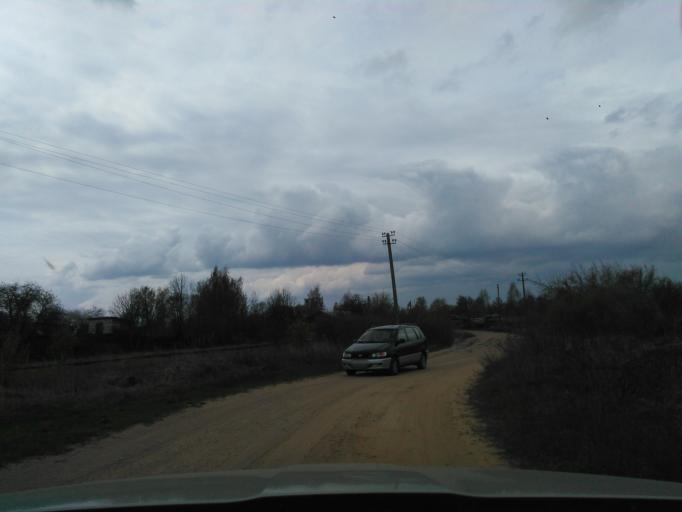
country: BY
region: Vitebsk
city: Chashniki
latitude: 54.8428
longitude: 29.1851
